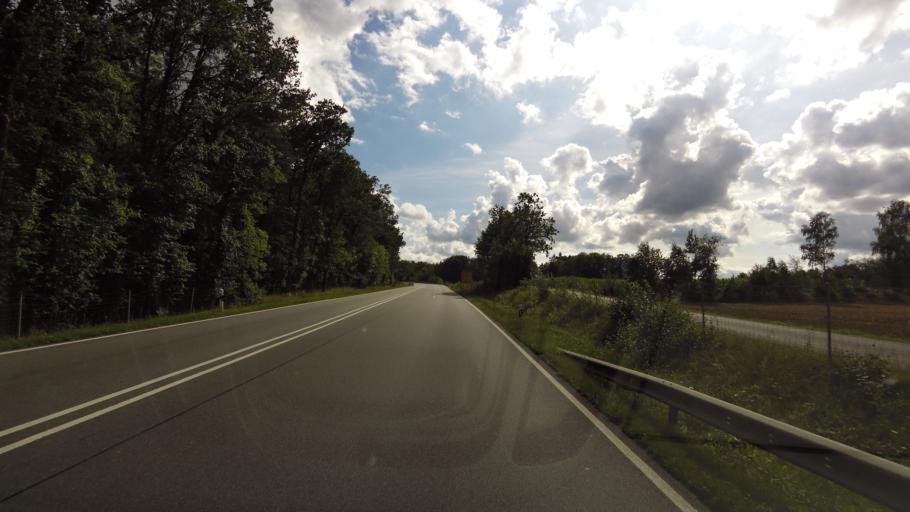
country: DE
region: Bavaria
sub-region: Upper Palatinate
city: Traitsching
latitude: 49.1811
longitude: 12.6512
